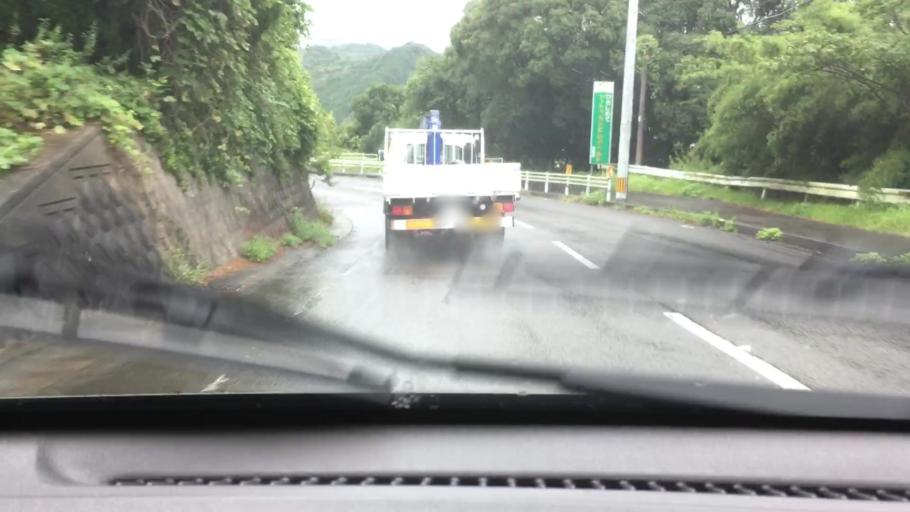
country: JP
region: Nagasaki
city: Togitsu
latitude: 32.8559
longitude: 129.7805
